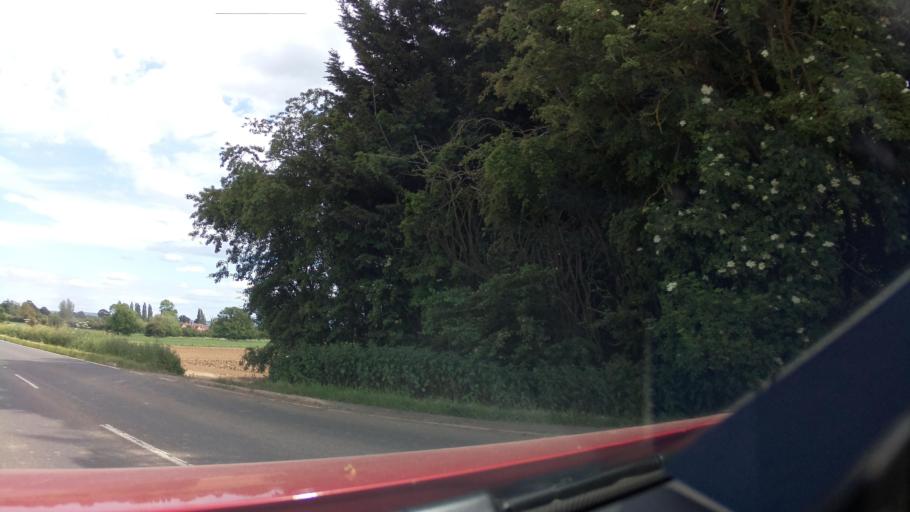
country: GB
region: England
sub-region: Worcestershire
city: Pershore
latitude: 52.1019
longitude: -2.0375
